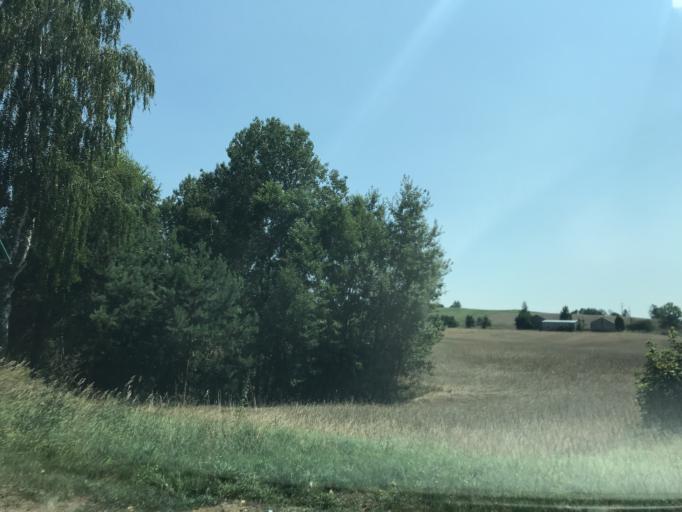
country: PL
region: Kujawsko-Pomorskie
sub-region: Powiat lipnowski
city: Chrostkowo
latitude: 52.9495
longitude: 19.2178
